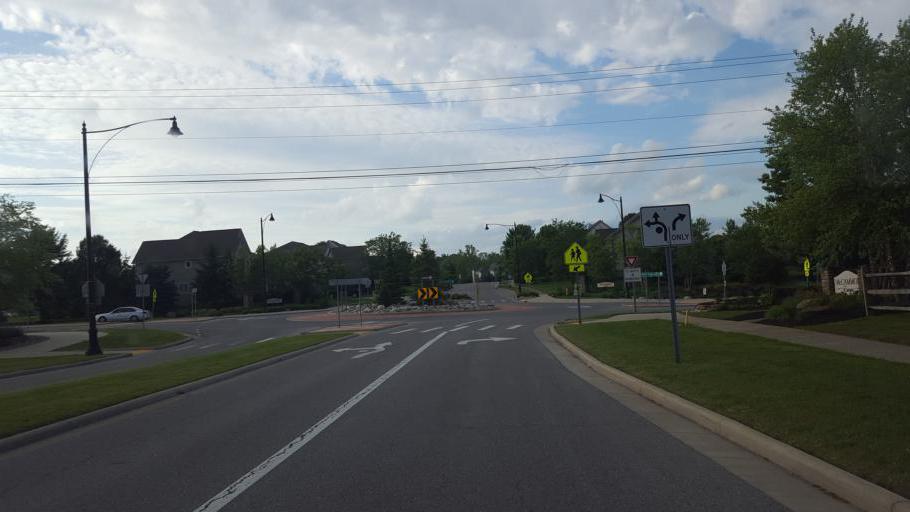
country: US
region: Ohio
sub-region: Delaware County
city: Lewis Center
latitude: 40.1726
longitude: -82.9732
